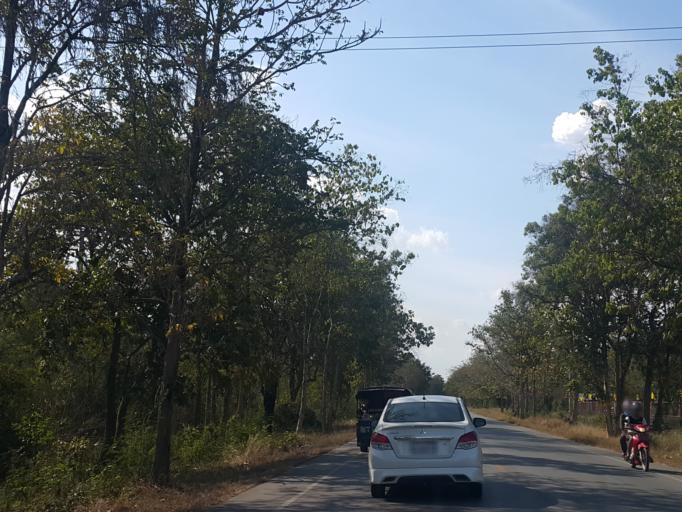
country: TH
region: Sukhothai
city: Sawankhalok
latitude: 17.3097
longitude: 99.7190
